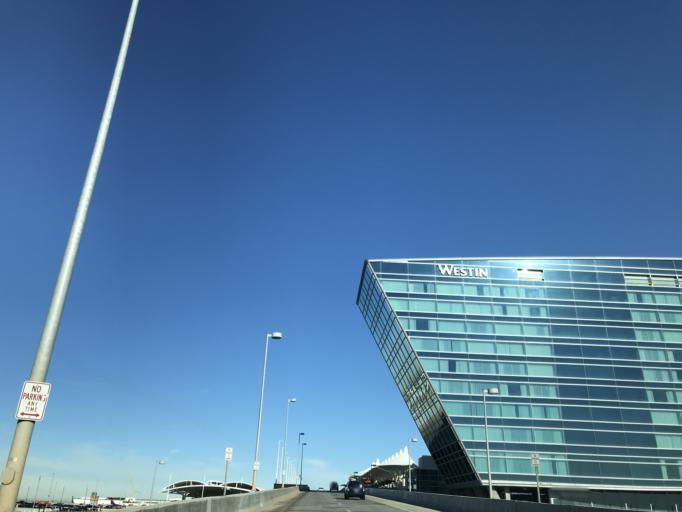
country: US
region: Colorado
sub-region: Weld County
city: Lochbuie
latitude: 39.8468
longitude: -104.6751
